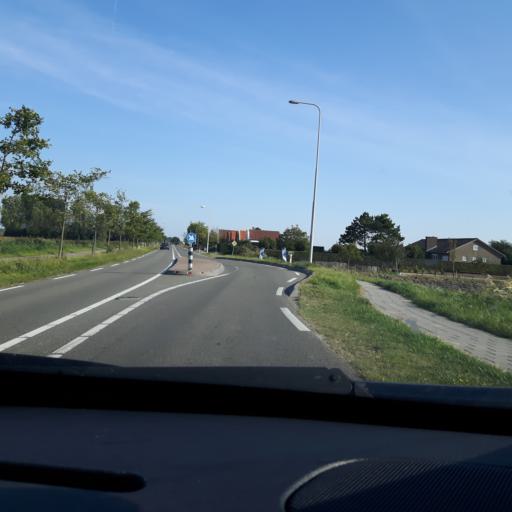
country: NL
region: Zeeland
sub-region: Gemeente Sluis
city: Sluis
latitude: 51.3382
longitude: 3.4550
